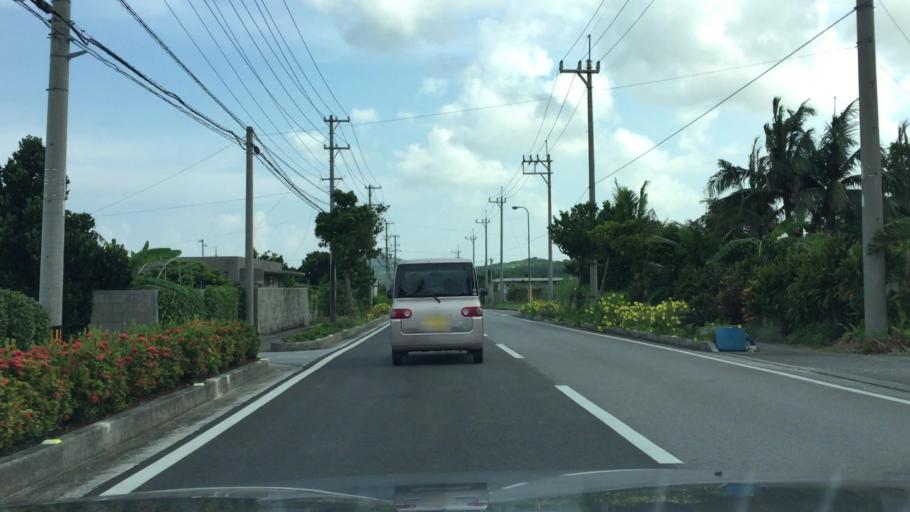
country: JP
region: Okinawa
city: Ishigaki
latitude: 24.4398
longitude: 124.2492
